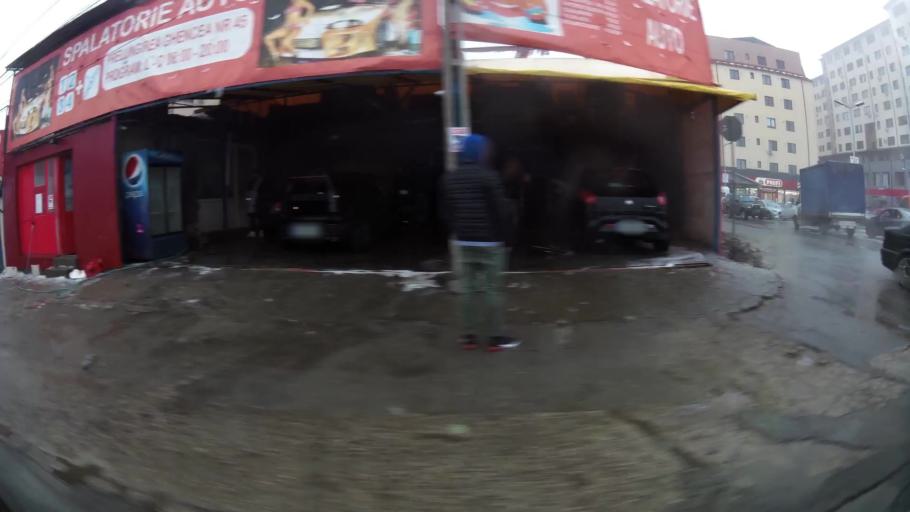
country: RO
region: Ilfov
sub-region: Comuna Bragadiru
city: Bragadiru
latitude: 44.4077
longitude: 25.9902
